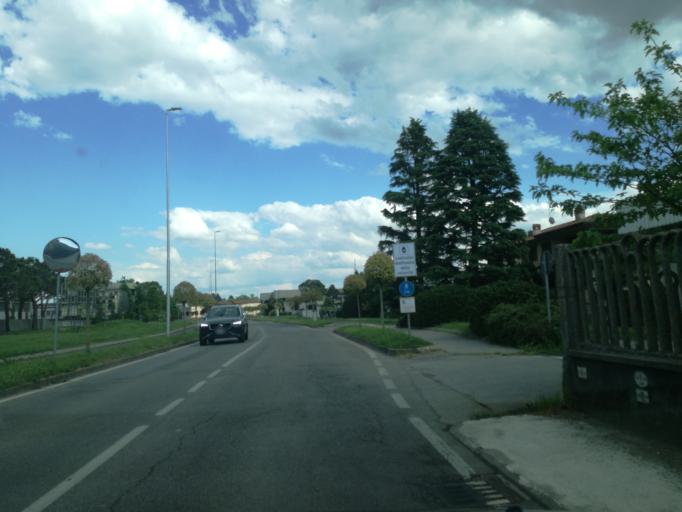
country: IT
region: Lombardy
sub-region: Provincia di Monza e Brianza
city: Ronco Briantino
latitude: 45.6652
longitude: 9.4104
